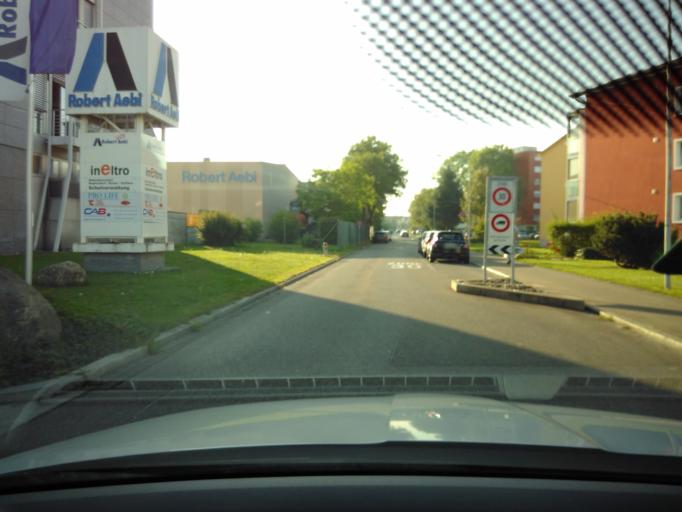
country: CH
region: Zurich
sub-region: Bezirk Dielsdorf
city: Regensdorf / Feldblumen-Riedthofstrasse
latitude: 47.4381
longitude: 8.4654
